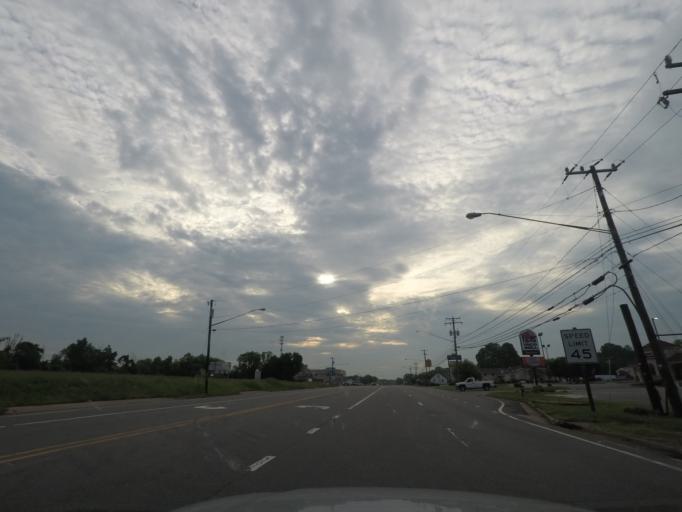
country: US
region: Virginia
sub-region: Halifax County
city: South Boston
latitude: 36.6875
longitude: -78.8991
